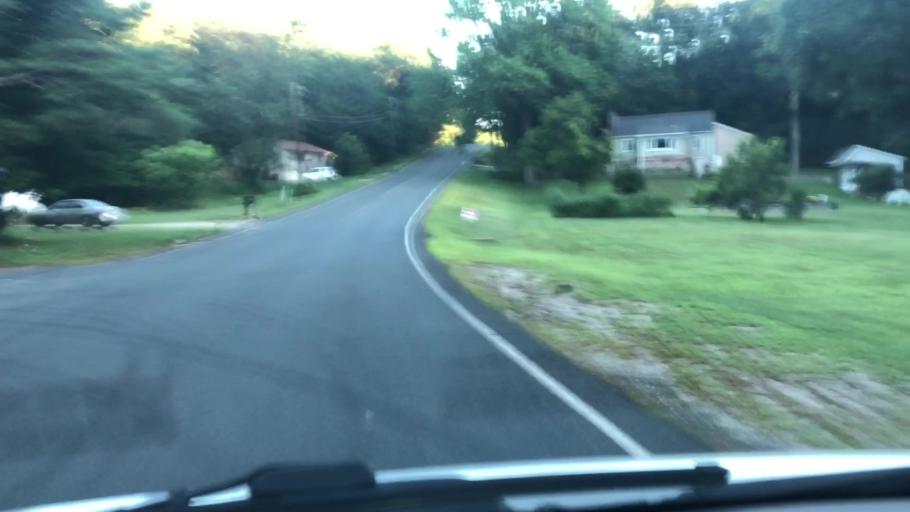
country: US
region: Massachusetts
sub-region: Hampshire County
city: Westhampton
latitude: 42.2721
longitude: -72.7485
